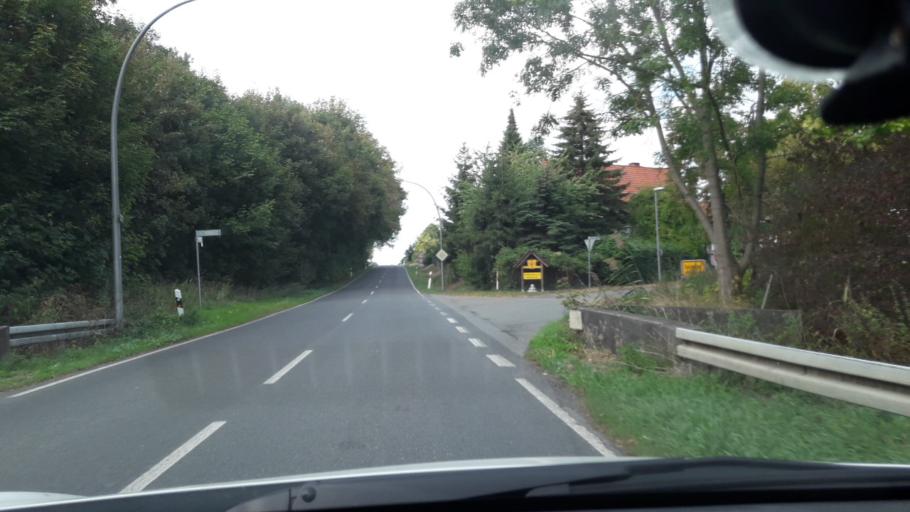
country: DE
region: Lower Saxony
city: Alt Wallmoden
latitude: 52.0236
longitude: 10.3509
